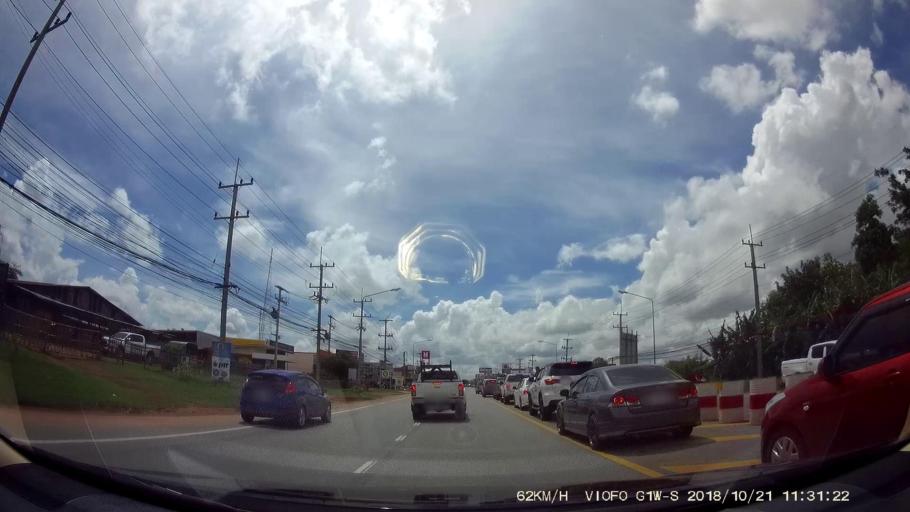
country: TH
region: Chaiyaphum
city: Chaiyaphum
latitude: 15.7697
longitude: 102.0256
